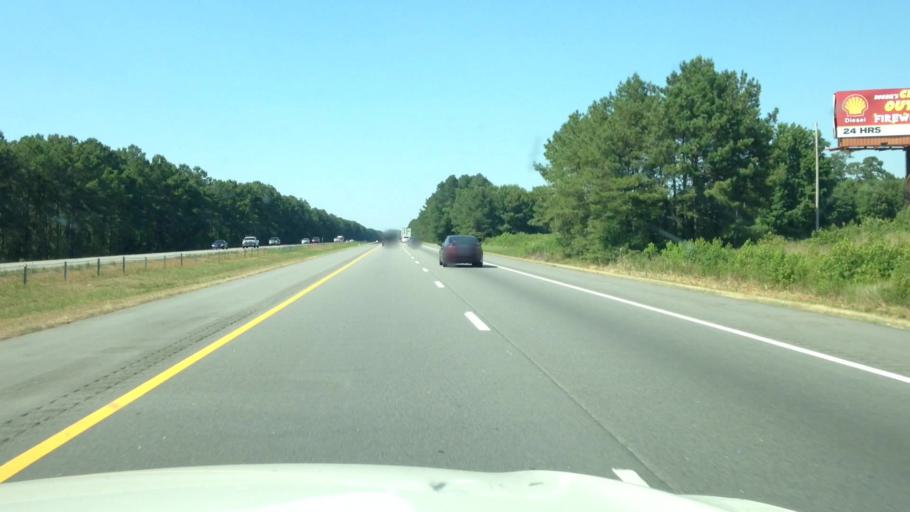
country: US
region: North Carolina
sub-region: Nash County
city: Red Oak
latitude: 36.0408
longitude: -77.8341
